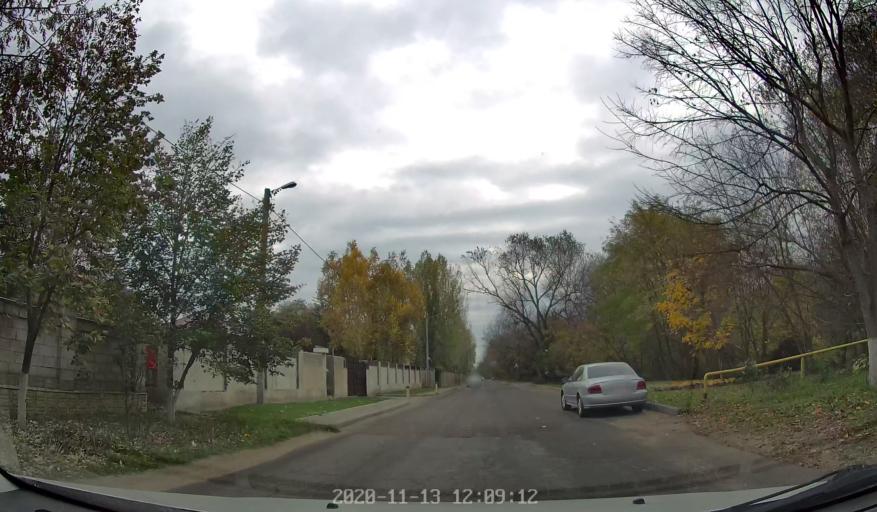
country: MD
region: Chisinau
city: Chisinau
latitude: 46.9603
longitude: 28.8356
